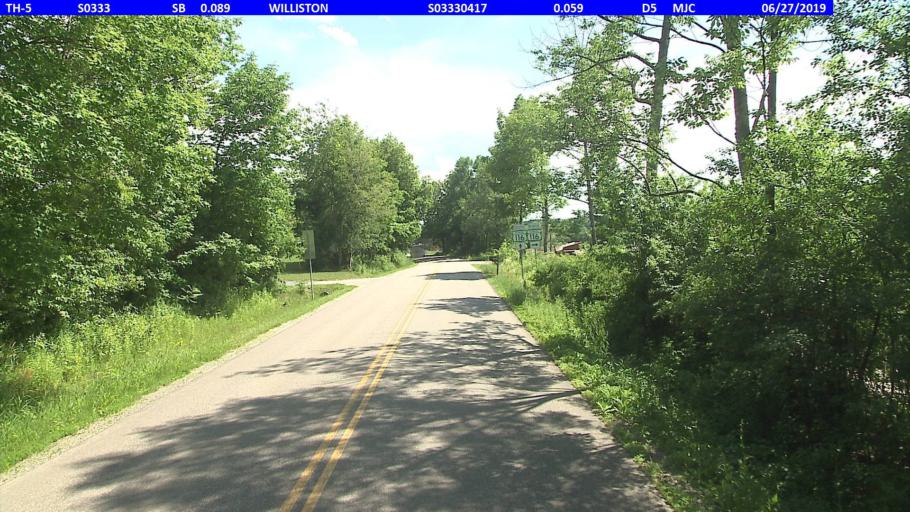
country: US
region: Vermont
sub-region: Chittenden County
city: South Burlington
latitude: 44.4024
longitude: -73.1407
